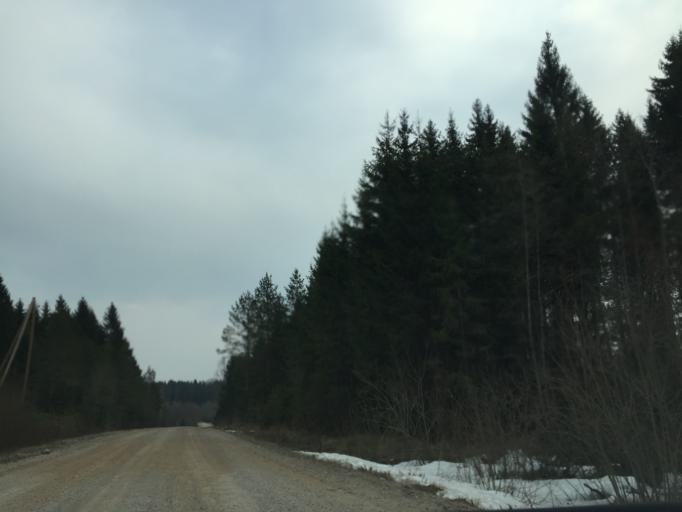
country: LV
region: Priekuli
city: Priekuli
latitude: 57.1704
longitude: 25.4933
